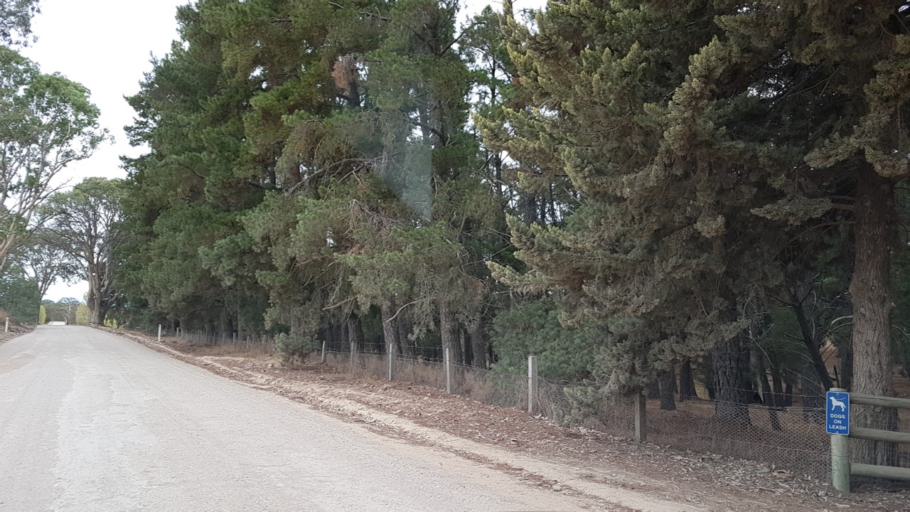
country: AU
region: South Australia
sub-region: Mount Barker
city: Nairne
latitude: -34.9567
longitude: 139.0107
